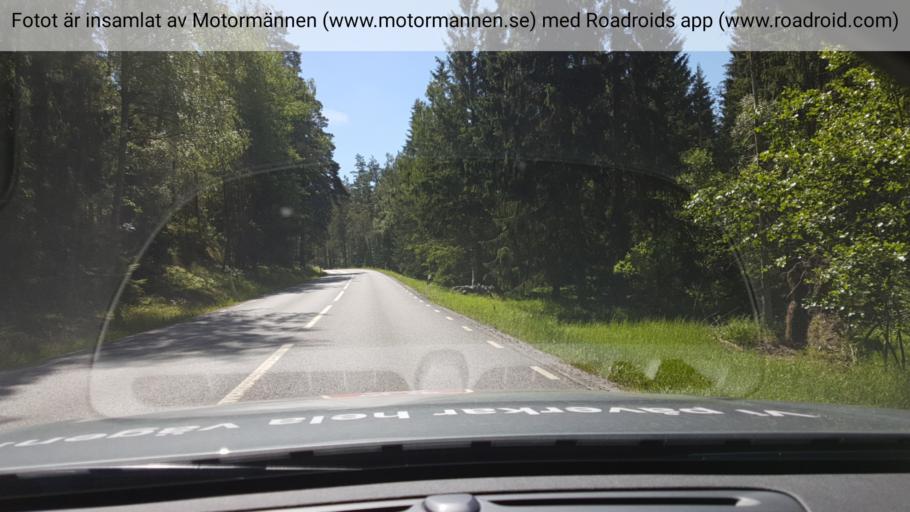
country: SE
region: Stockholm
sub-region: Haninge Kommun
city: Haninge
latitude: 59.1482
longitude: 18.1801
